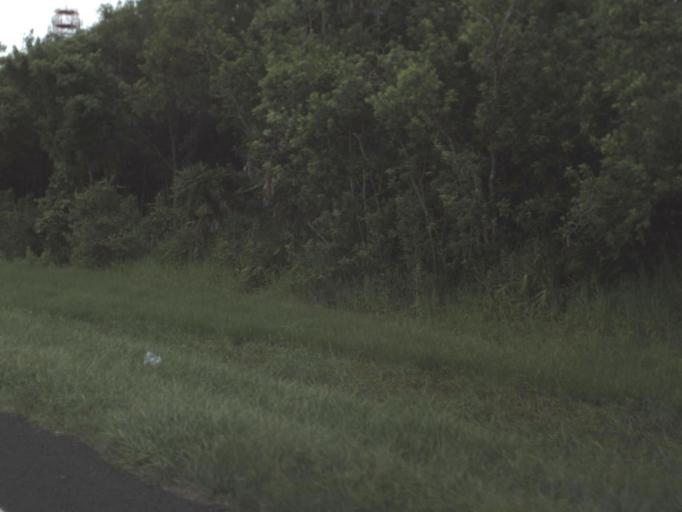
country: US
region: Florida
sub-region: Hillsborough County
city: Sun City Center
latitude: 27.7192
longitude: -82.3353
